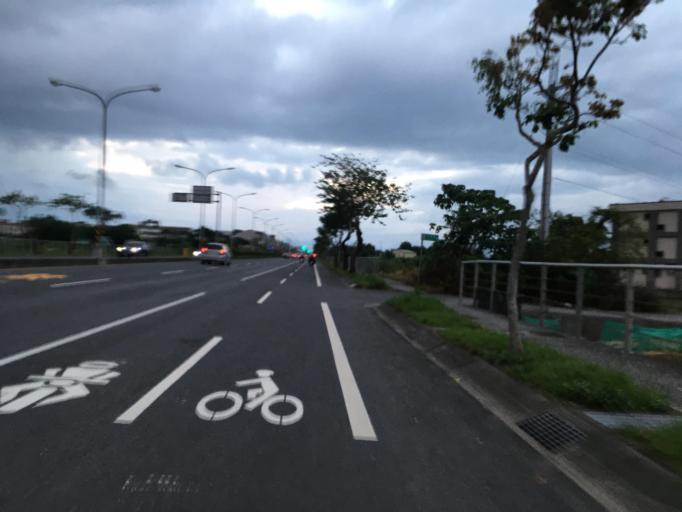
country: TW
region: Taiwan
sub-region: Yilan
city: Yilan
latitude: 24.6193
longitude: 121.8437
